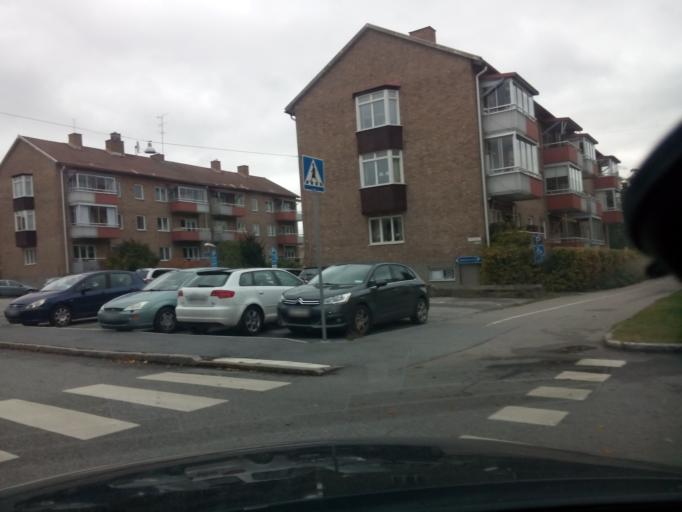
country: SE
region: Soedermanland
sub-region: Nykopings Kommun
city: Nykoping
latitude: 58.7564
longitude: 17.0174
